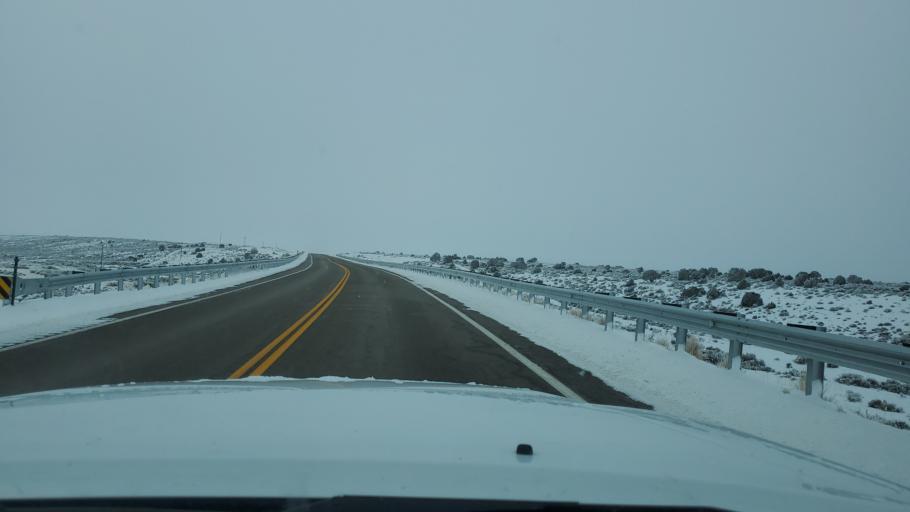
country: US
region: Colorado
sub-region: Rio Blanco County
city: Rangely
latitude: 40.3335
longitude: -108.4908
